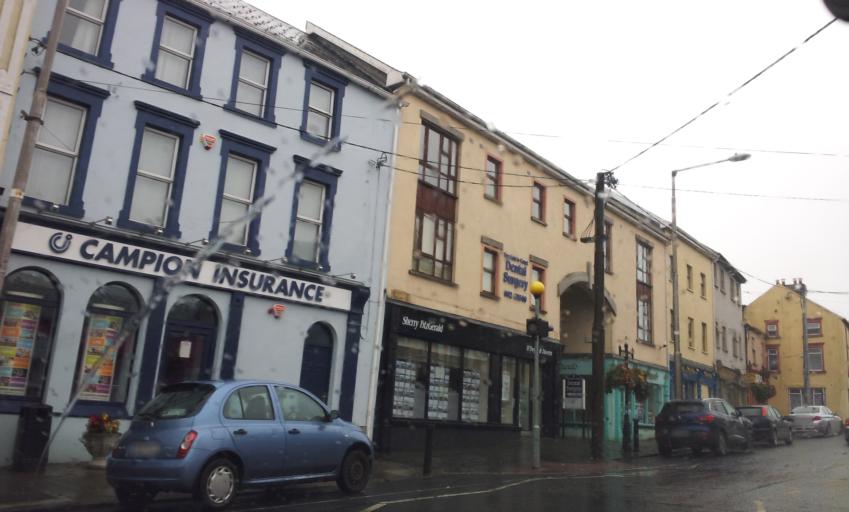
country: IE
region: Munster
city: Cashel
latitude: 52.5175
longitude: -7.8868
